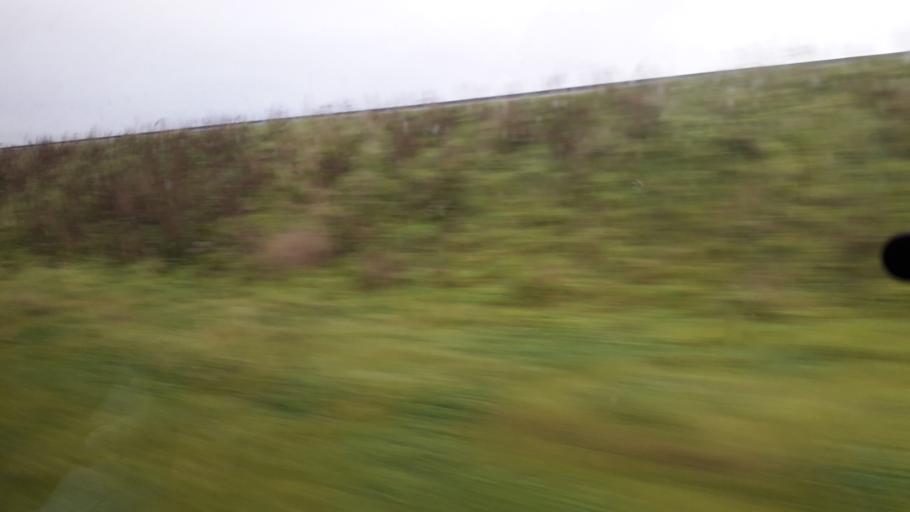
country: IE
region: Connaught
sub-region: County Galway
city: Athenry
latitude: 53.2927
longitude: -8.8084
